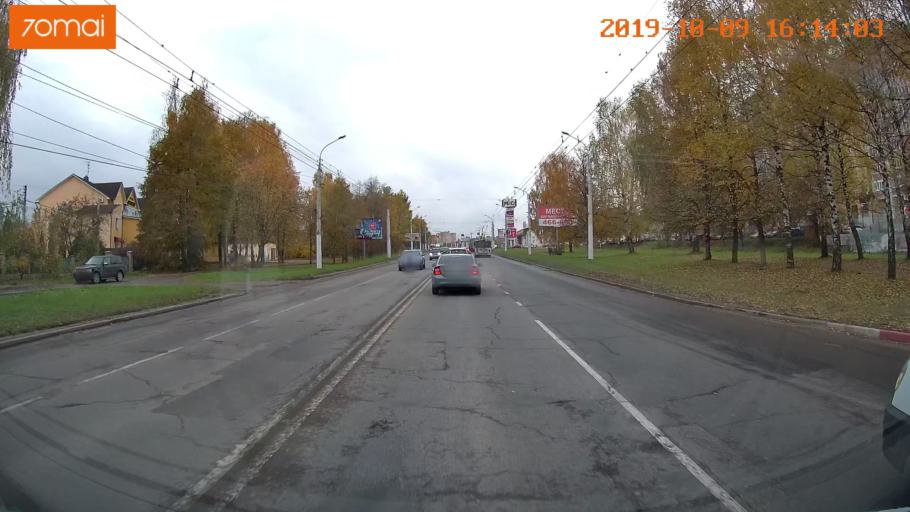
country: RU
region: Kostroma
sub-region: Kostromskoy Rayon
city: Kostroma
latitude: 57.7437
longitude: 40.9238
